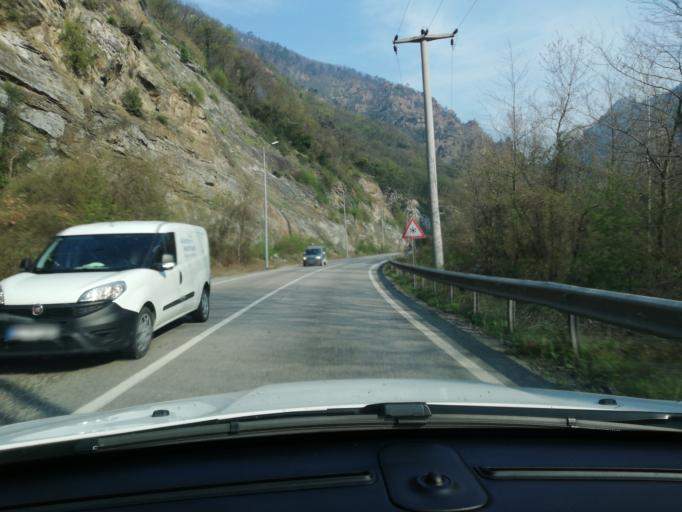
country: TR
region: Karabuk
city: Yenice
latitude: 41.1728
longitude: 32.4469
